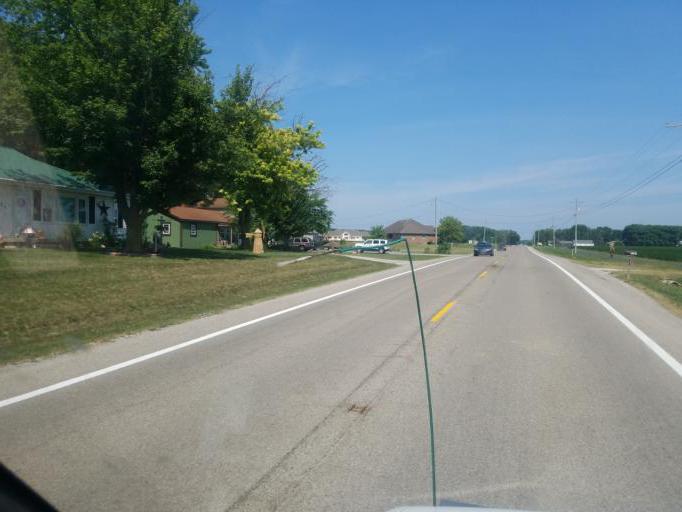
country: US
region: Ohio
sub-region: Mercer County
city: Celina
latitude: 40.5020
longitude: -84.5176
